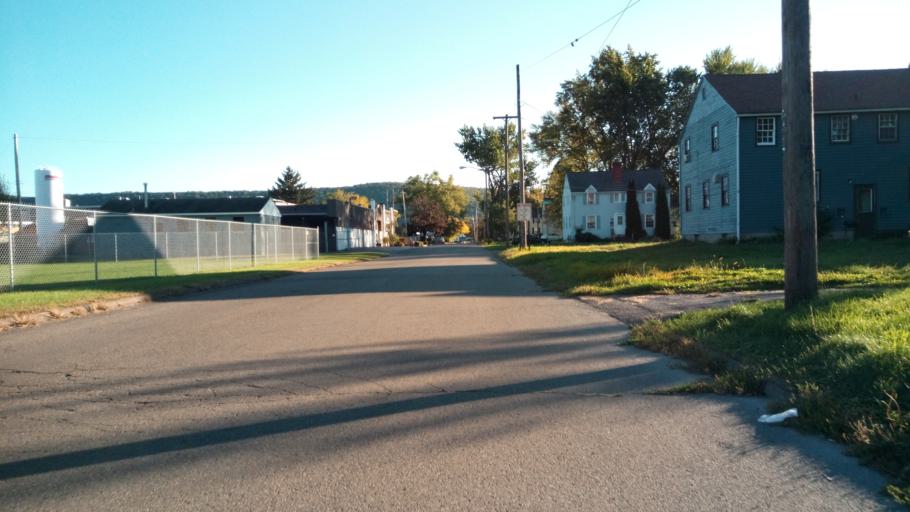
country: US
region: New York
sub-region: Chemung County
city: Southport
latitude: 42.0674
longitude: -76.8049
